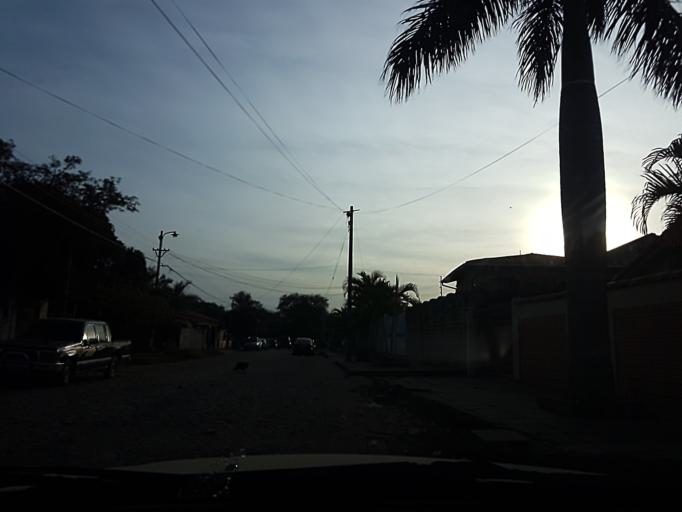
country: PY
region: Central
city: Colonia Mariano Roque Alonso
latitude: -25.2083
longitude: -57.5395
